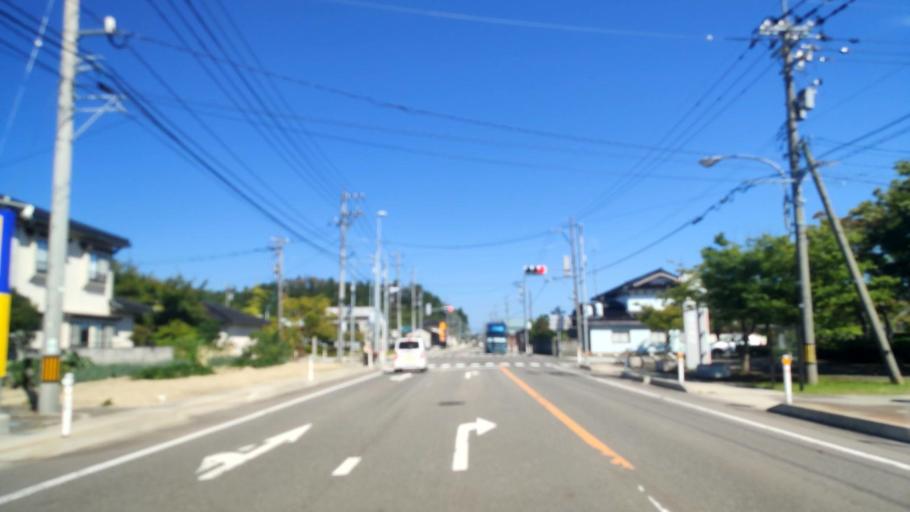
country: JP
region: Ishikawa
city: Nanao
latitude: 37.4445
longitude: 137.2688
